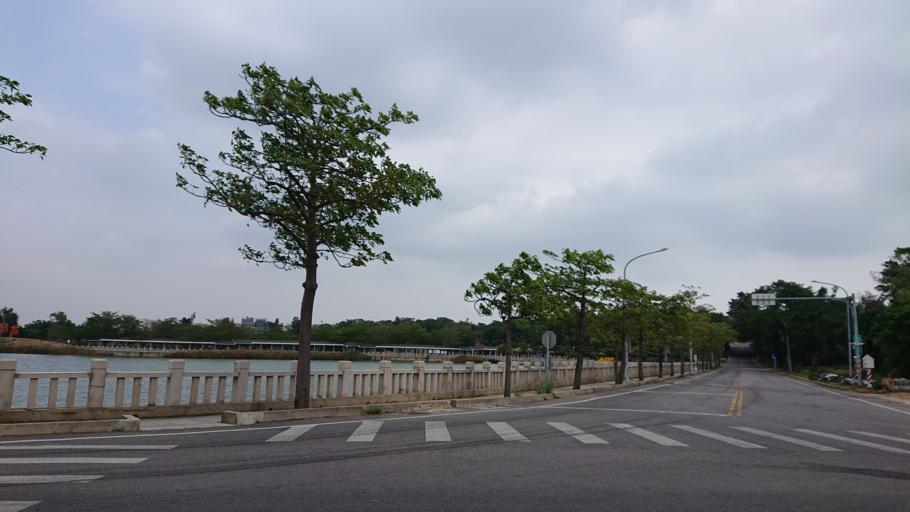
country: TW
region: Fukien
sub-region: Kinmen
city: Jincheng
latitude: 24.4267
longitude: 118.3156
